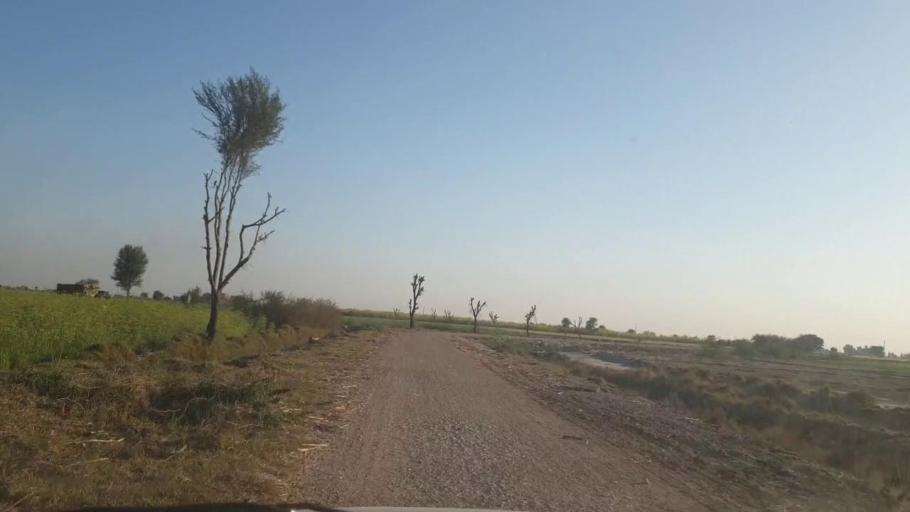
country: PK
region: Sindh
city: Mirpur Khas
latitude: 25.4645
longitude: 69.1125
